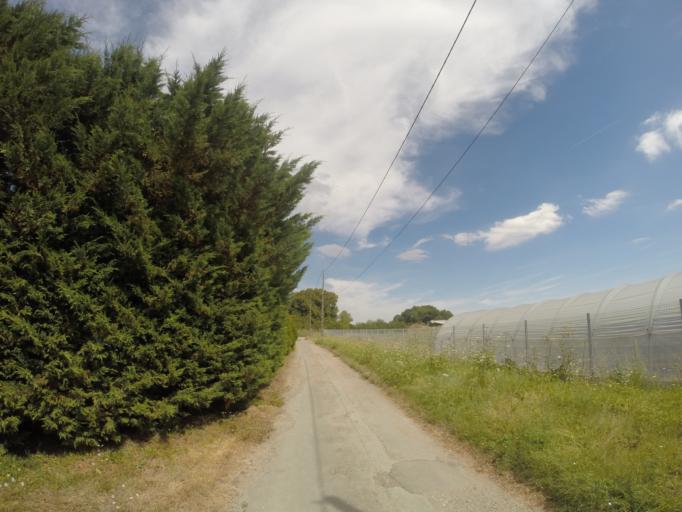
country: FR
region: Centre
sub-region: Departement d'Indre-et-Loire
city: Rochecorbon
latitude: 47.4196
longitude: 0.7190
